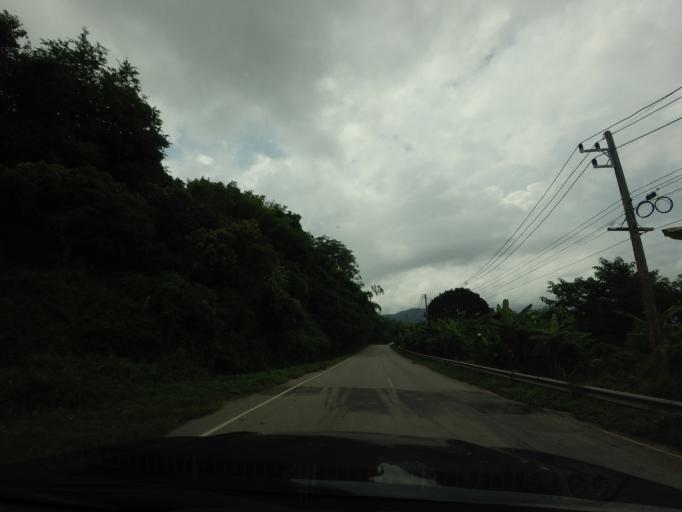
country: TH
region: Loei
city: Pak Chom
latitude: 18.0534
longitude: 101.8170
